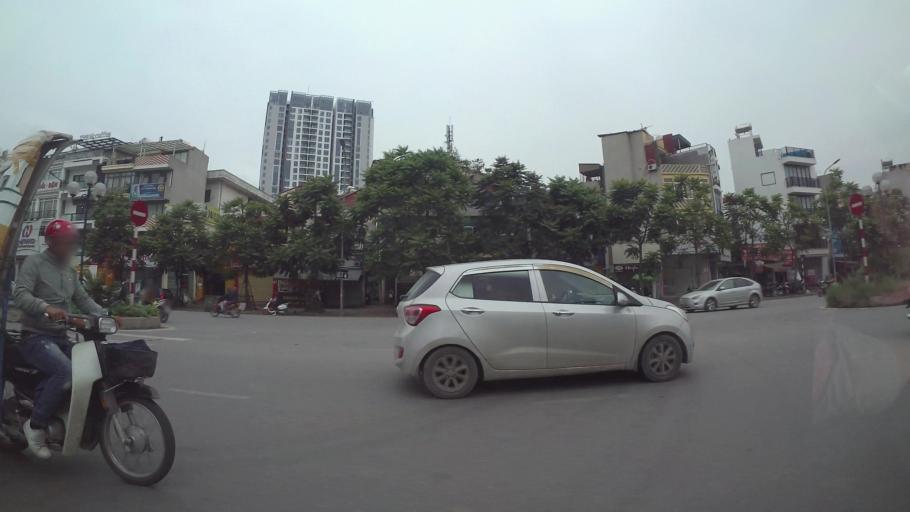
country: VN
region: Ha Noi
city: Hai BaTrung
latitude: 21.0087
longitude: 105.8643
